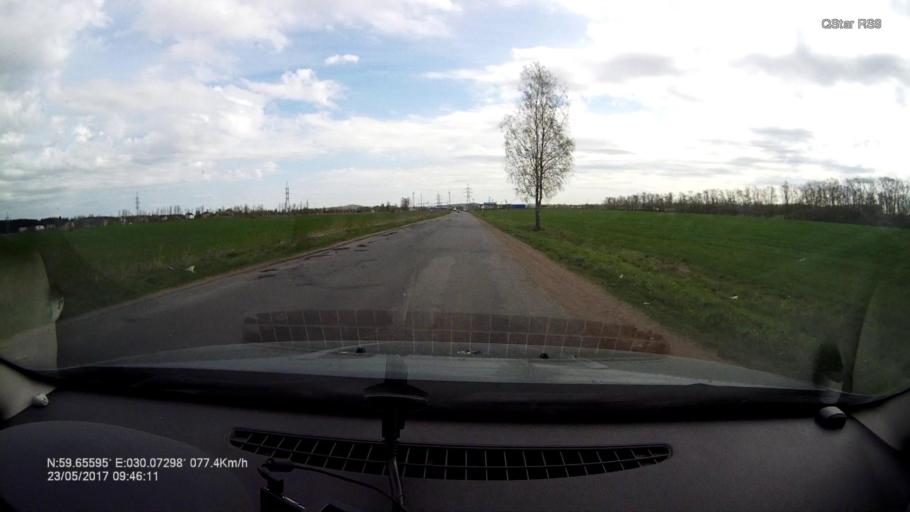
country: RU
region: Leningrad
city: Taytsy
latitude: 59.6559
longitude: 30.0730
